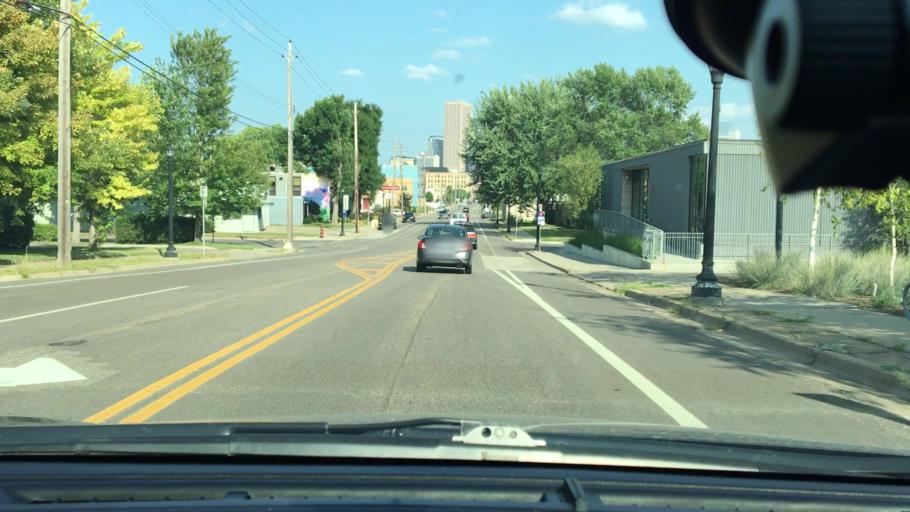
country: US
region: Minnesota
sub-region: Hennepin County
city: Minneapolis
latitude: 44.9807
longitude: -93.2980
